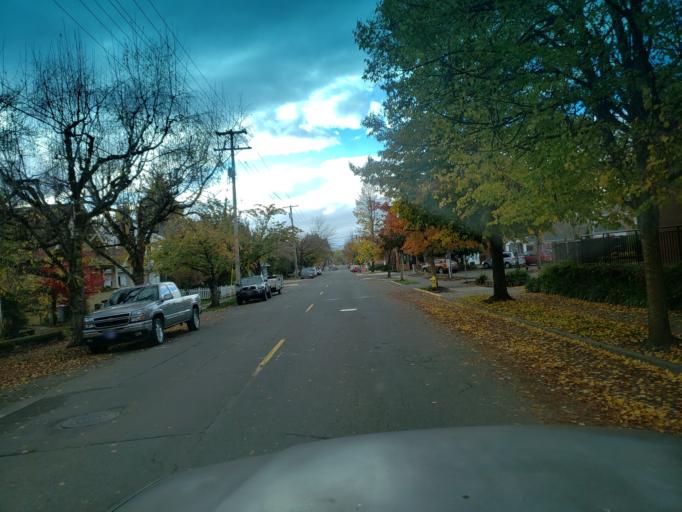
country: US
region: Oregon
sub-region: Yamhill County
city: McMinnville
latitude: 45.2086
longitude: -123.1936
